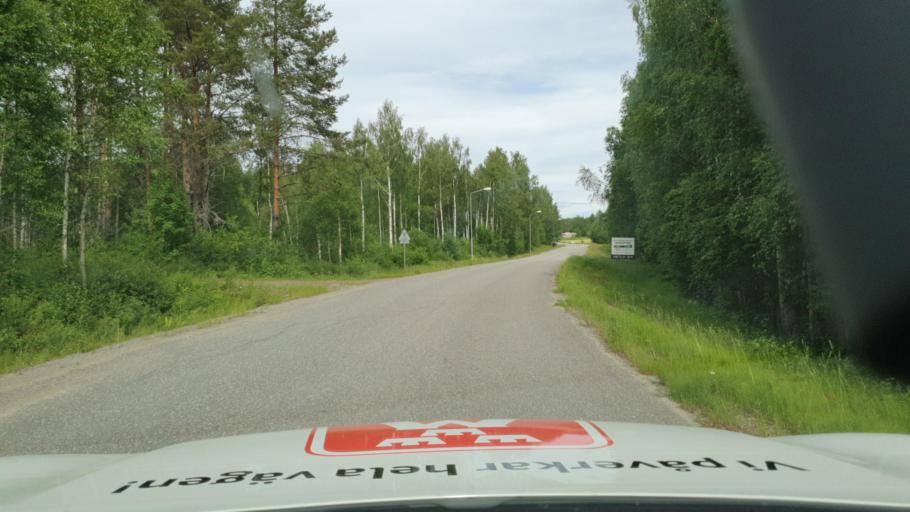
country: SE
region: Vaesterbotten
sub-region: Skelleftea Kommun
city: Viken
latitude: 64.5182
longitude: 20.9529
